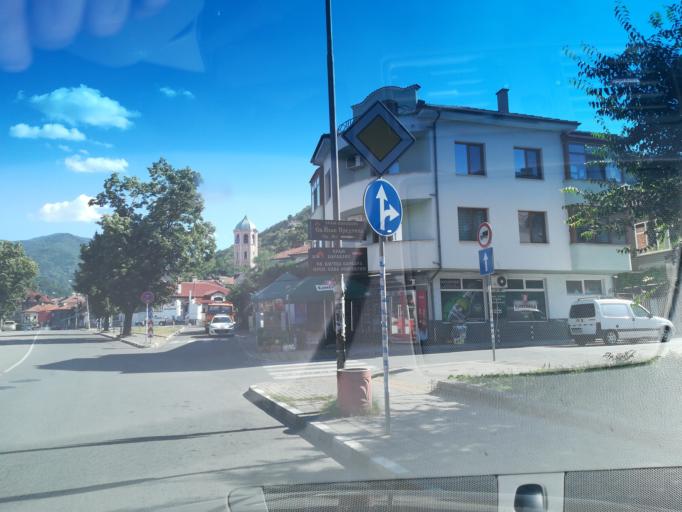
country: BG
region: Plovdiv
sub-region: Obshtina Asenovgrad
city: Asenovgrad
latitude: 42.0048
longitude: 24.8705
